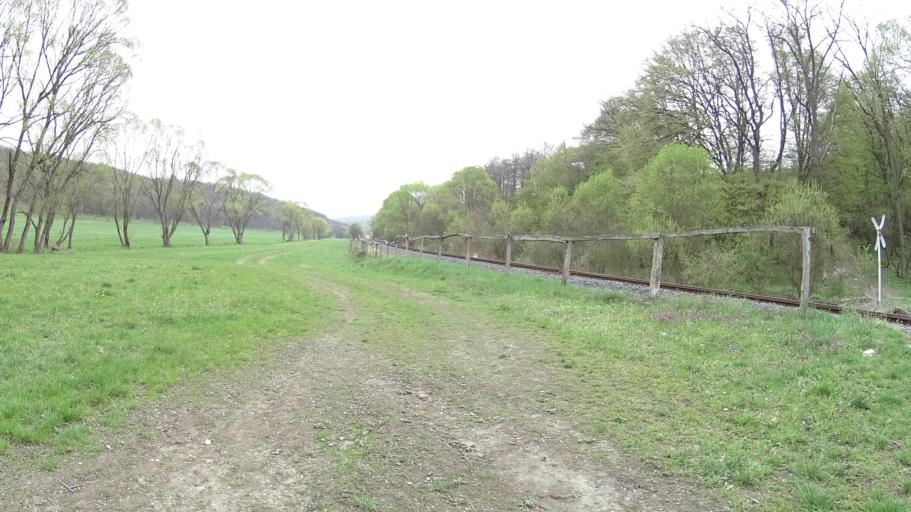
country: HU
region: Nograd
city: Diosjeno
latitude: 47.8879
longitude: 19.0510
